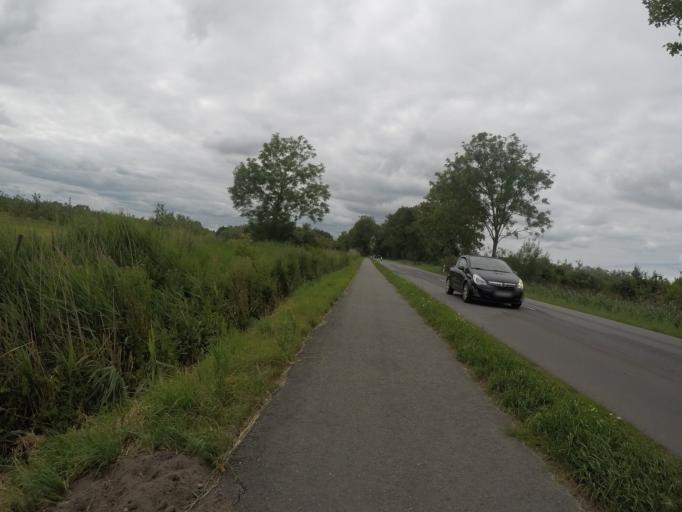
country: DE
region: Lower Saxony
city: Grossenworden
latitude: 53.6713
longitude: 9.2940
